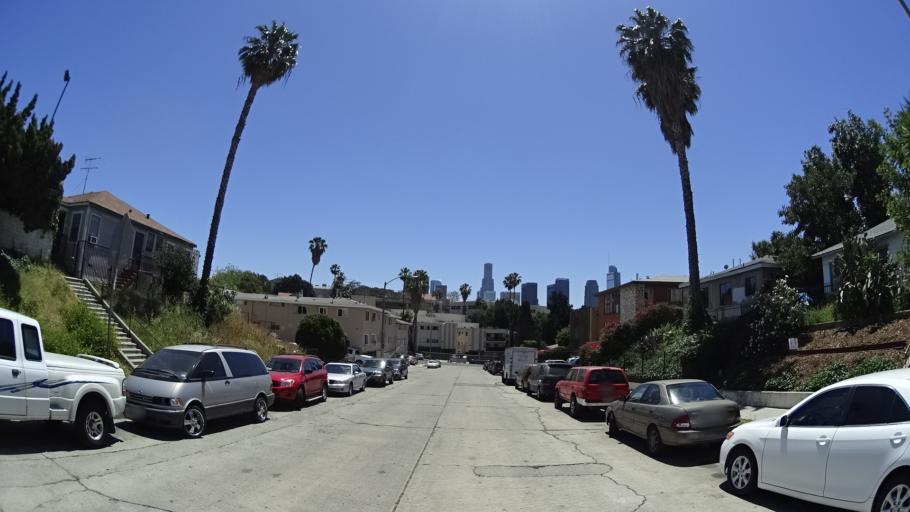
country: US
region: California
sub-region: Los Angeles County
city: Echo Park
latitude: 34.0634
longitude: -118.2659
